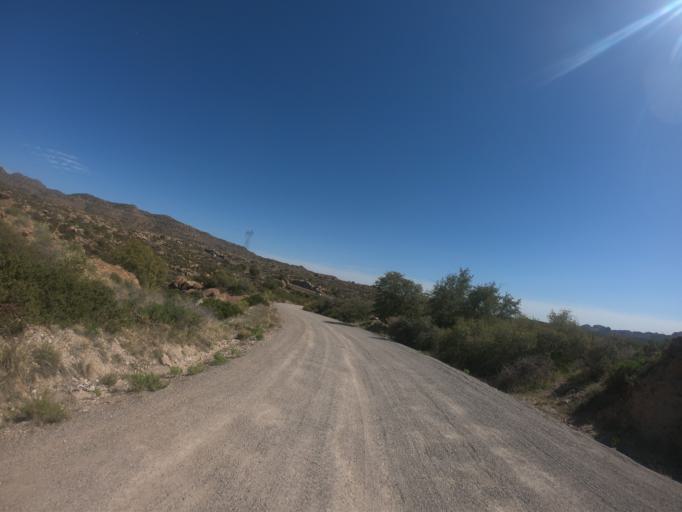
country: US
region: Arizona
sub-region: Pinal County
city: Superior
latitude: 33.3157
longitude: -111.0430
